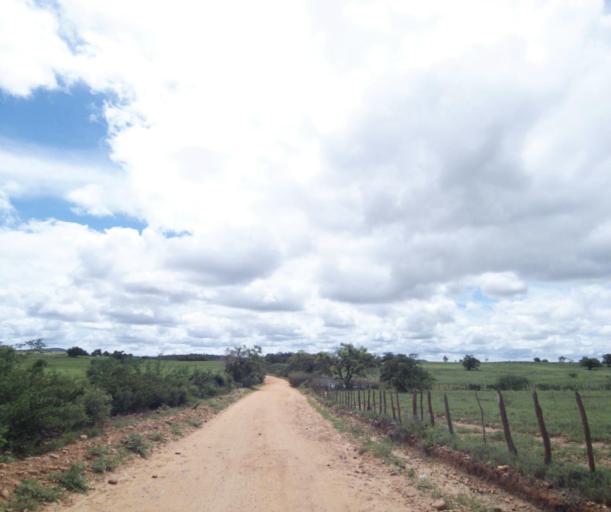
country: BR
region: Bahia
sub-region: Tanhacu
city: Tanhacu
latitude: -14.1547
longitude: -41.1974
